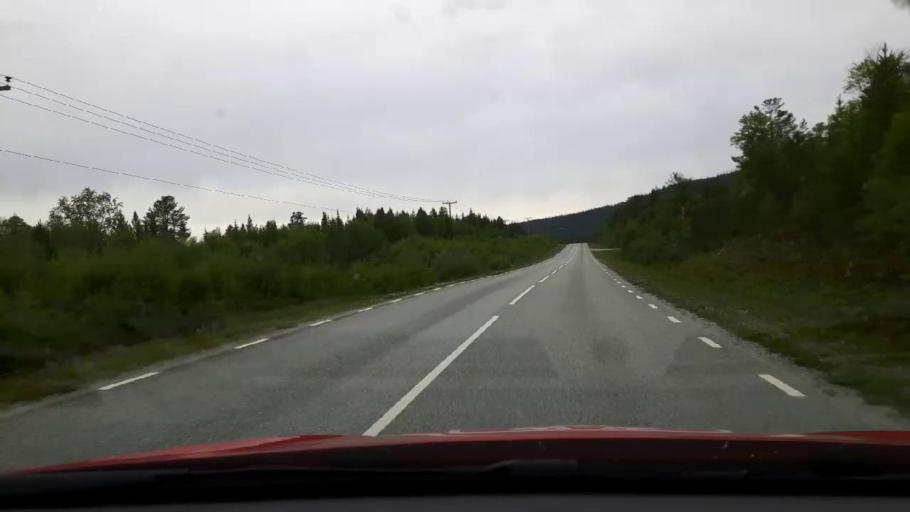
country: SE
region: Jaemtland
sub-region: Are Kommun
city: Are
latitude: 62.5715
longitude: 12.5604
